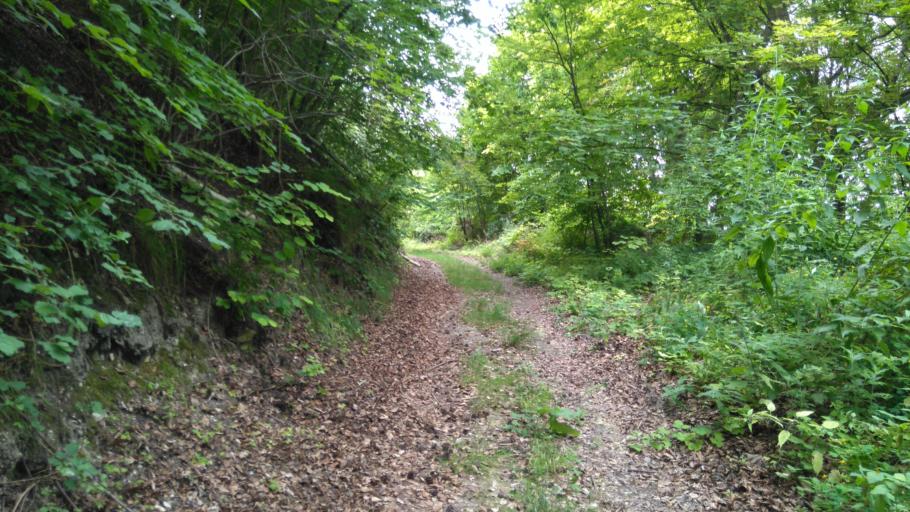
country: FR
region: Picardie
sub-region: Departement de l'Oise
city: Saint-Maximin
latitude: 49.2418
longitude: 2.4534
